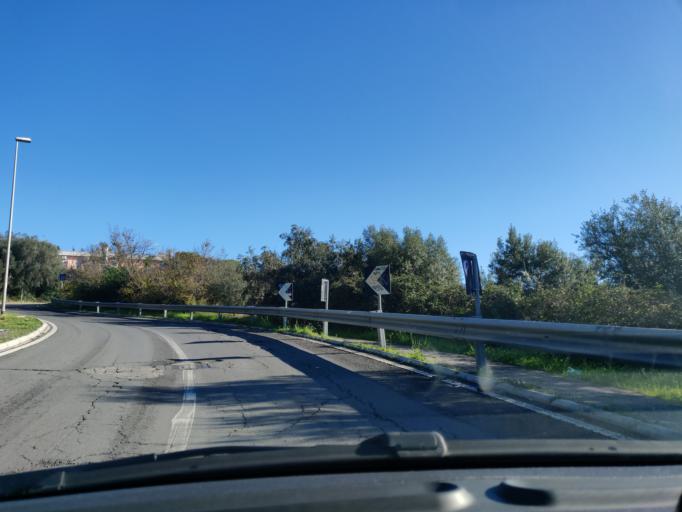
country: IT
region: Latium
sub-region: Citta metropolitana di Roma Capitale
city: Civitavecchia
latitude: 42.0951
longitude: 11.8189
